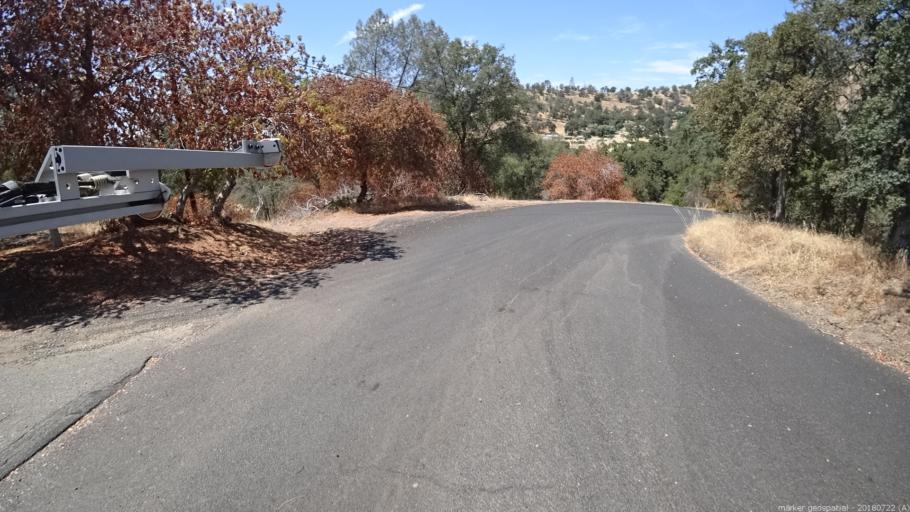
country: US
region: California
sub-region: Madera County
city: Yosemite Lakes
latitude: 37.2291
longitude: -119.7477
